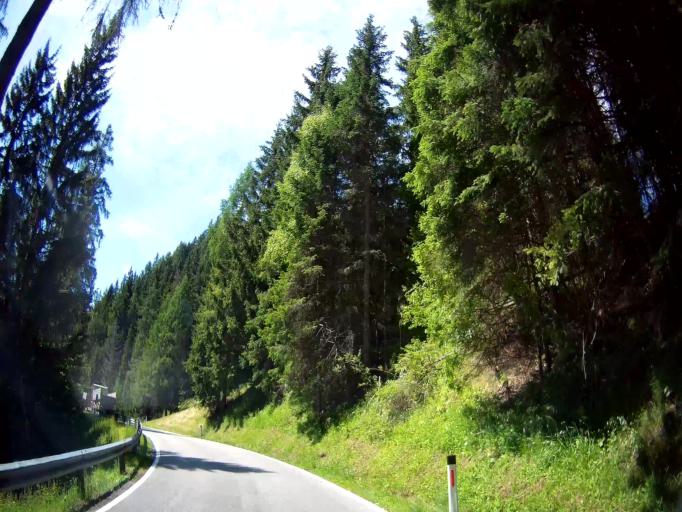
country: AT
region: Carinthia
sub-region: Politischer Bezirk Sankt Veit an der Glan
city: Glodnitz
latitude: 46.9365
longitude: 14.0539
